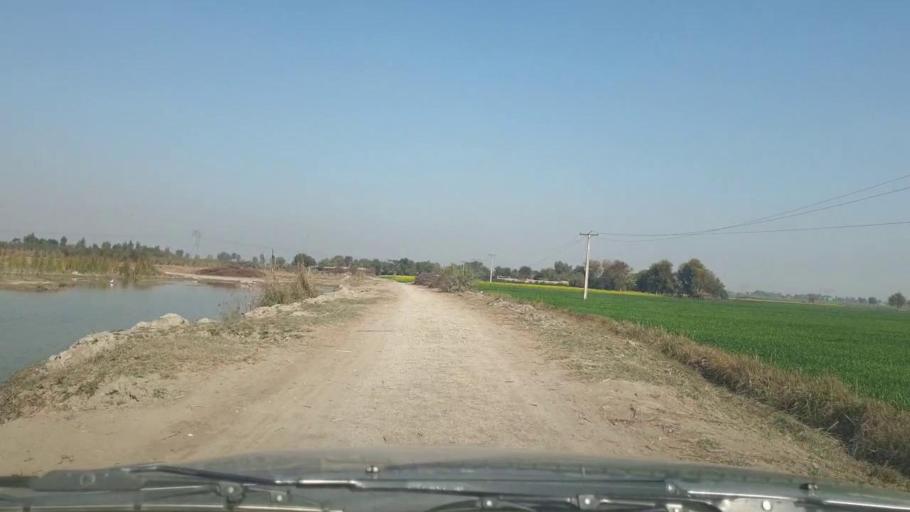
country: PK
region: Sindh
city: Mirpur Mathelo
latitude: 28.0450
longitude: 69.5619
